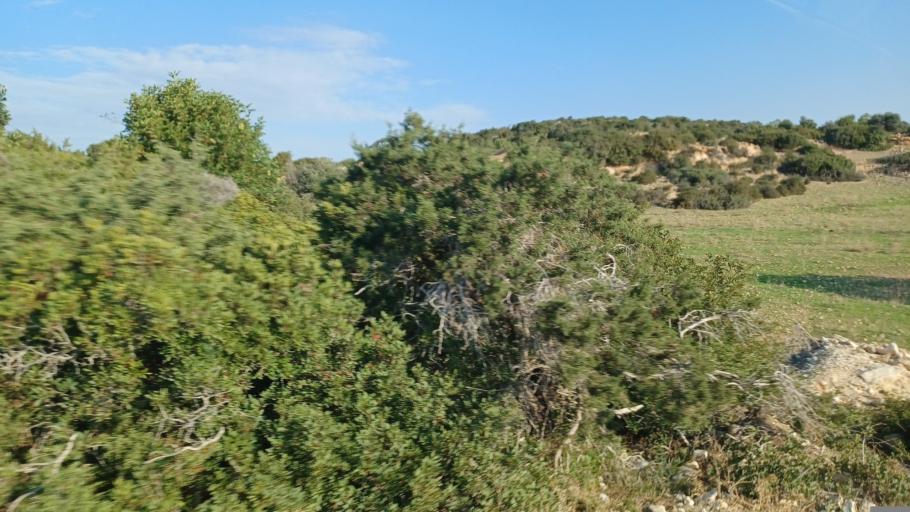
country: CY
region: Pafos
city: Pegeia
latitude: 34.9094
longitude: 32.3338
